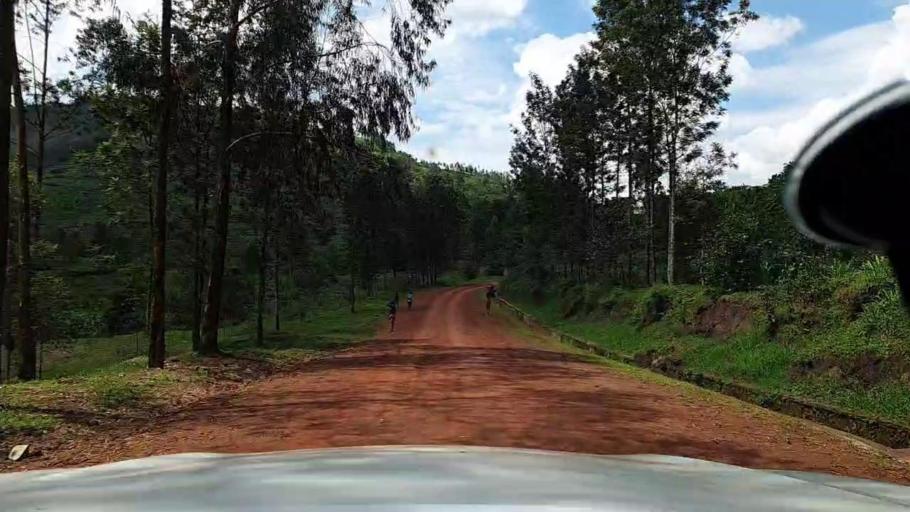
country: RW
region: Northern Province
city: Byumba
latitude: -1.7054
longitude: 29.8426
